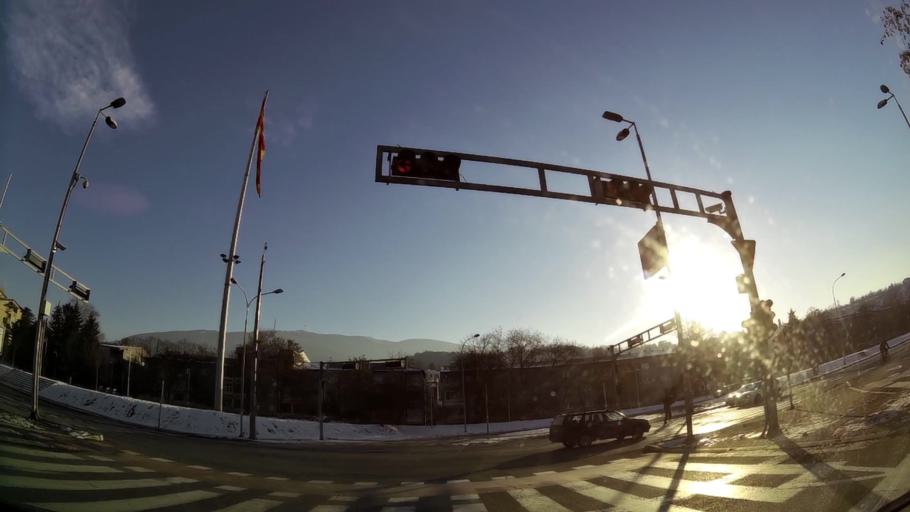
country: MK
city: Krushopek
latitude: 41.9985
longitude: 21.3890
